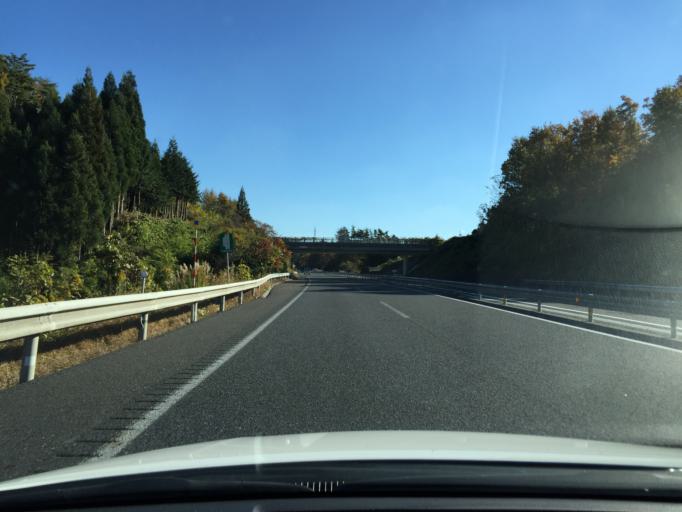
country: JP
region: Fukushima
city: Funehikimachi-funehiki
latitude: 37.4156
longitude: 140.5618
